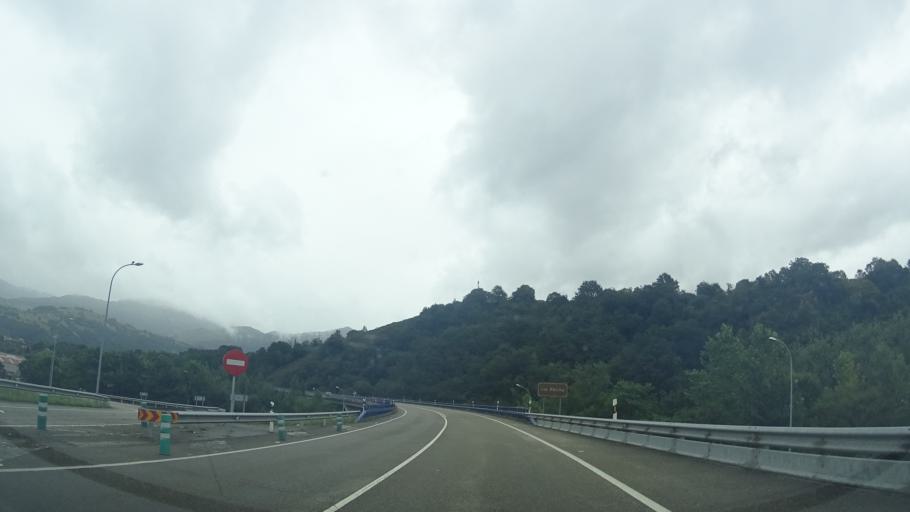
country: ES
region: Asturias
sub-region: Province of Asturias
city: Parres
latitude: 43.3748
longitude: -5.1813
